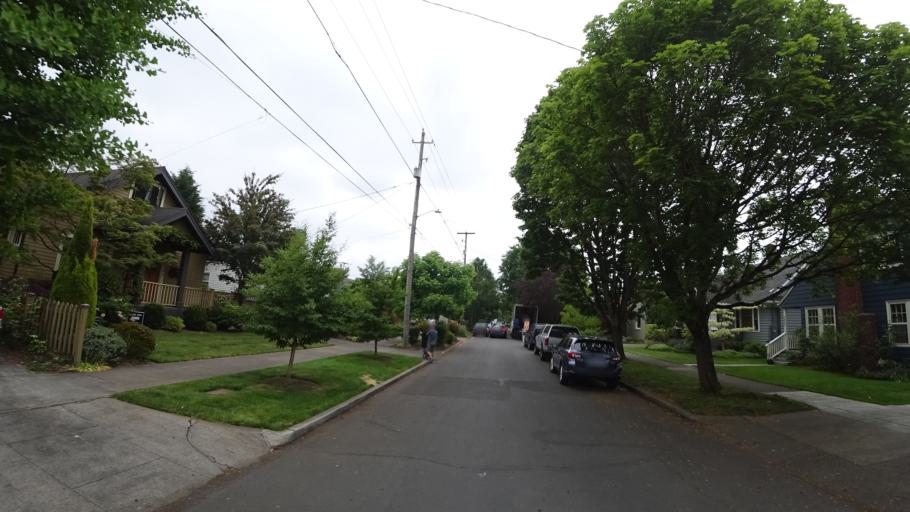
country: US
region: Oregon
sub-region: Multnomah County
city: Portland
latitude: 45.5478
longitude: -122.6147
